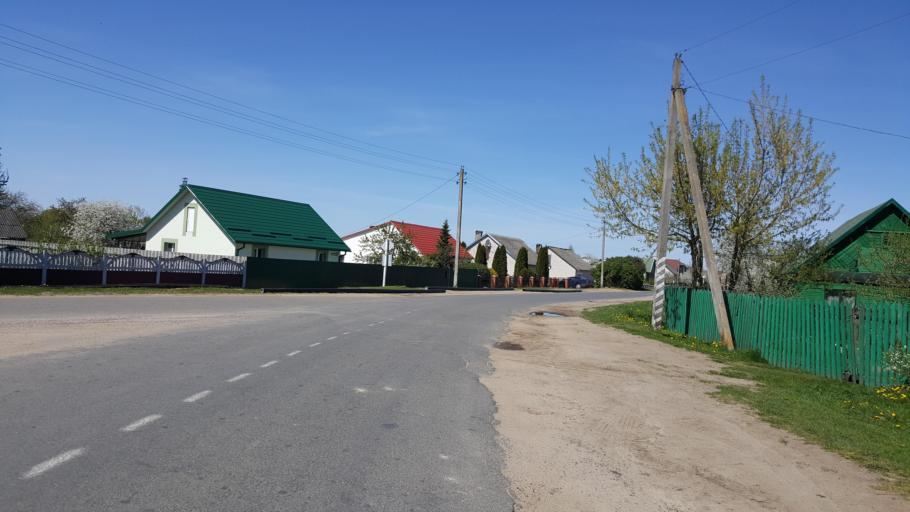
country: BY
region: Brest
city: Kamyanyets
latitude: 52.4453
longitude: 23.8461
